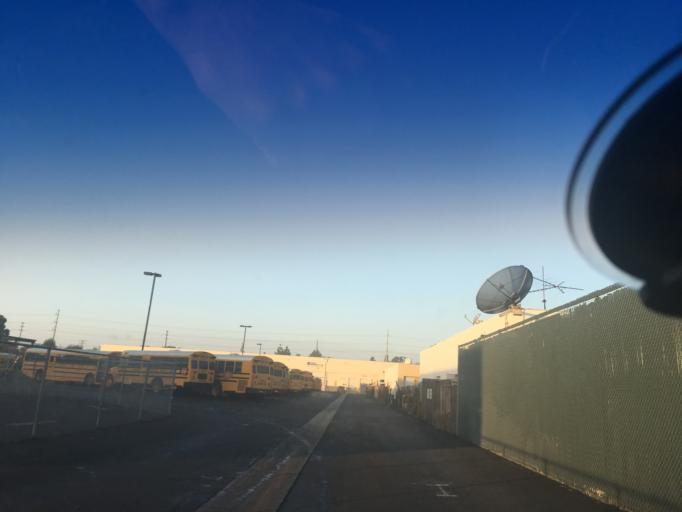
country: US
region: California
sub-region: Orange County
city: Anaheim
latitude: 33.8229
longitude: -117.8988
